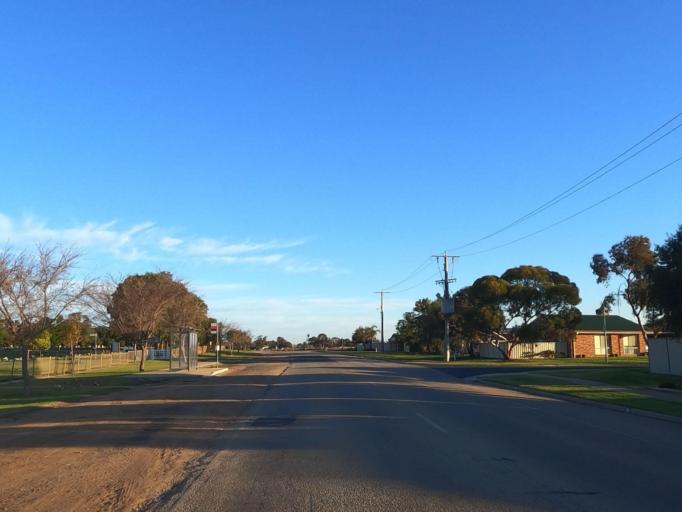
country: AU
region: Victoria
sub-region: Swan Hill
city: Swan Hill
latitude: -35.3533
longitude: 143.5531
